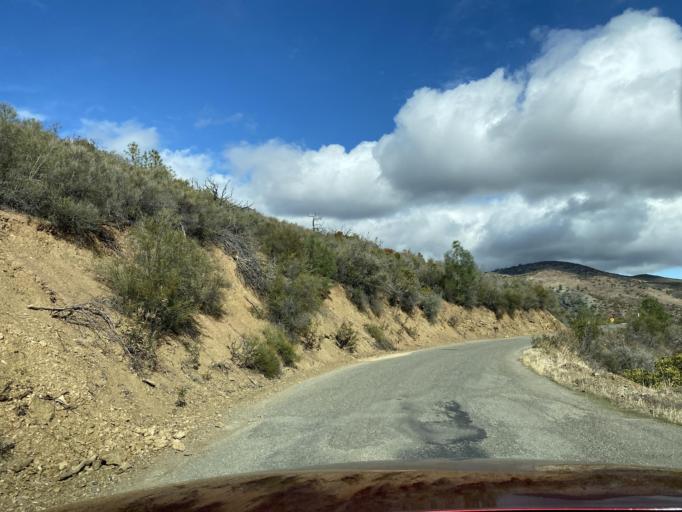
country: US
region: California
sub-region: Lake County
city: Lucerne
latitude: 39.3713
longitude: -122.6443
